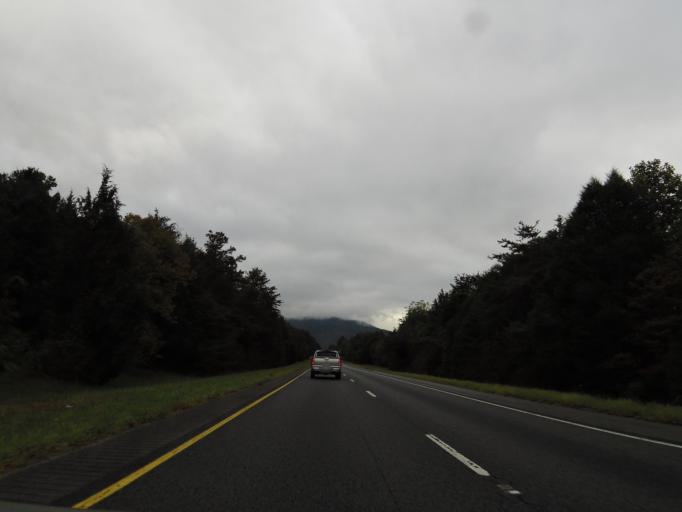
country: US
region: Georgia
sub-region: Dade County
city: Trenton
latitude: 34.9484
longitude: -85.4694
